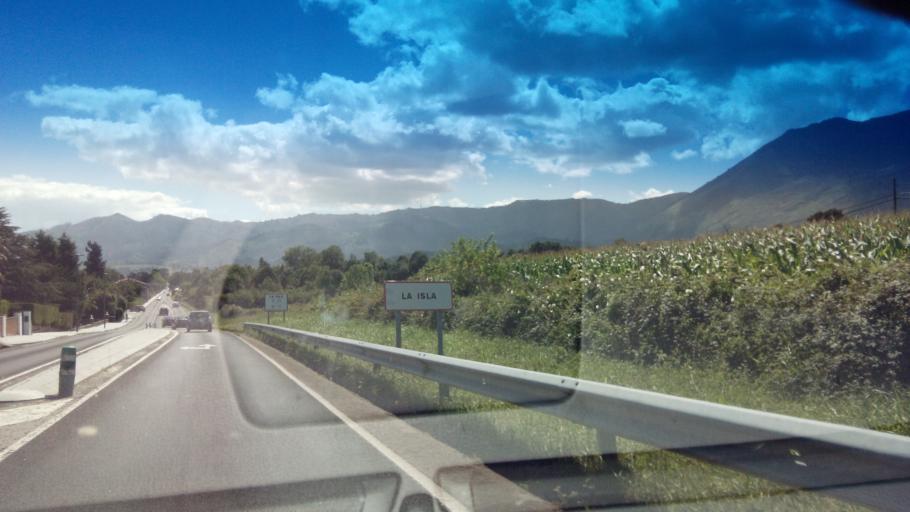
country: ES
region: Asturias
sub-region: Province of Asturias
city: Colunga
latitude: 43.4810
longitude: -5.2334
